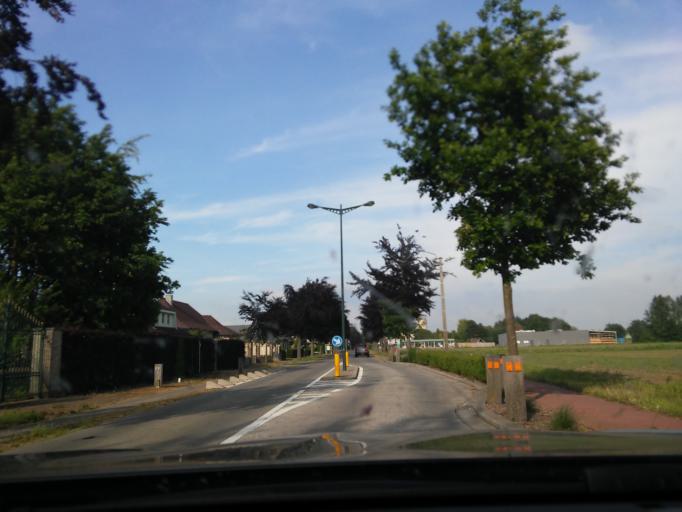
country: BE
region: Flanders
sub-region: Provincie Oost-Vlaanderen
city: Assenede
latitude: 51.2185
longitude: 3.7377
